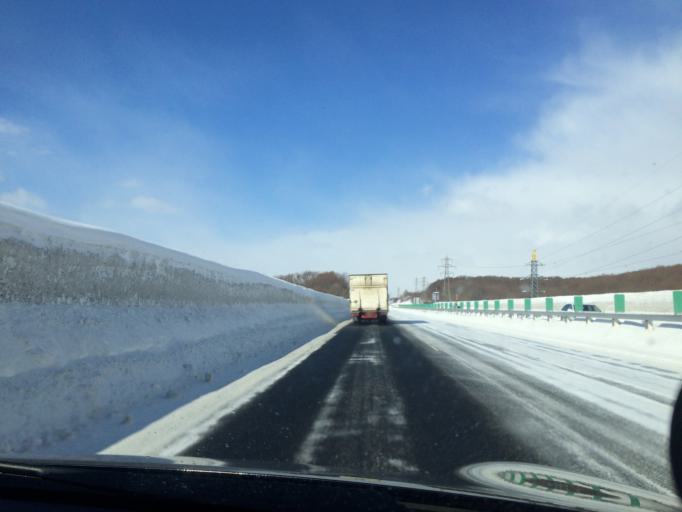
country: JP
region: Hokkaido
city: Kitahiroshima
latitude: 42.9573
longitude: 141.5046
